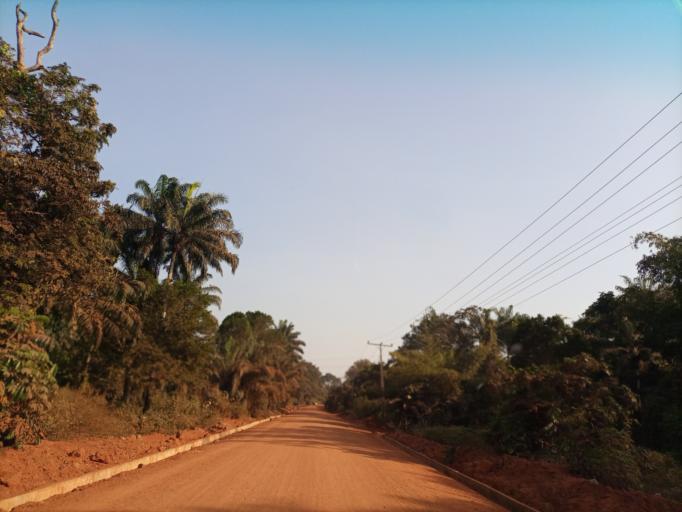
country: NG
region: Enugu
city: Opi
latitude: 6.7550
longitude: 7.4055
